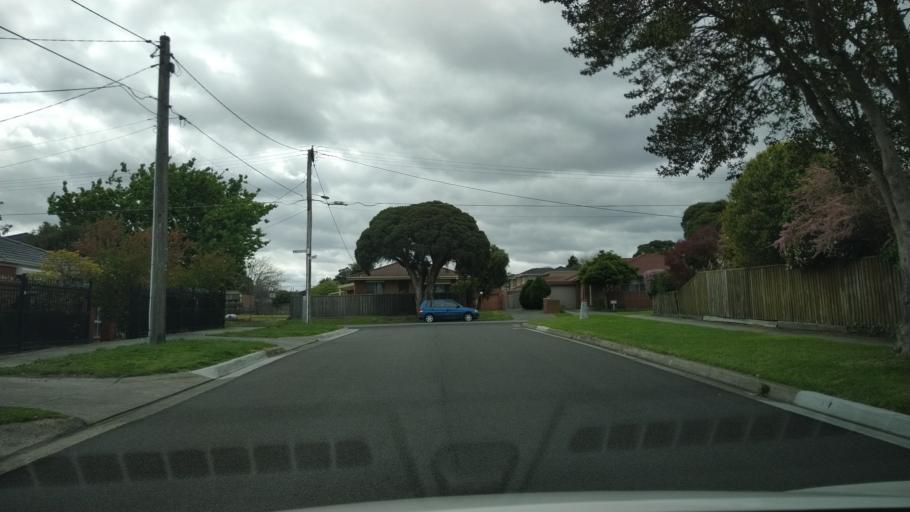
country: AU
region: Victoria
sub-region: Greater Dandenong
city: Noble Park
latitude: -37.9739
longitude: 145.1698
